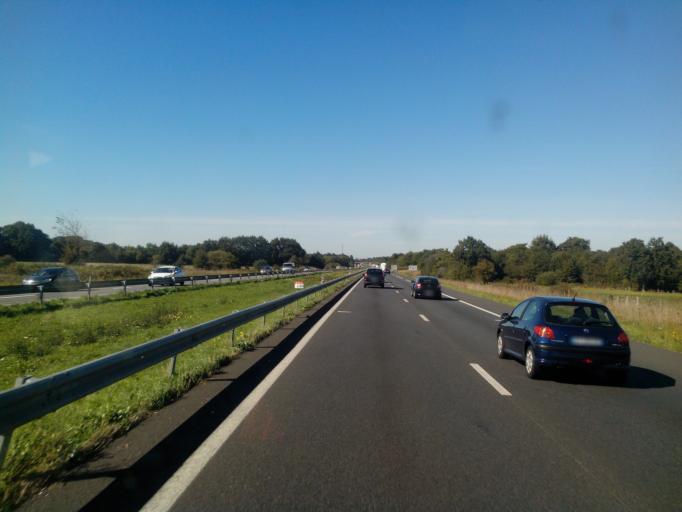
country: FR
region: Pays de la Loire
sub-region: Departement de la Loire-Atlantique
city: Le Temple-de-Bretagne
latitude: 47.3139
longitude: -1.7688
